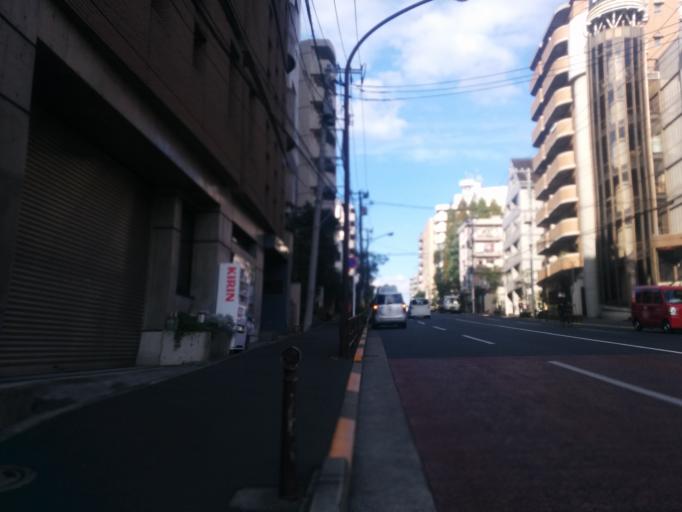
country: JP
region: Tokyo
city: Tokyo
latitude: 35.7084
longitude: 139.7459
